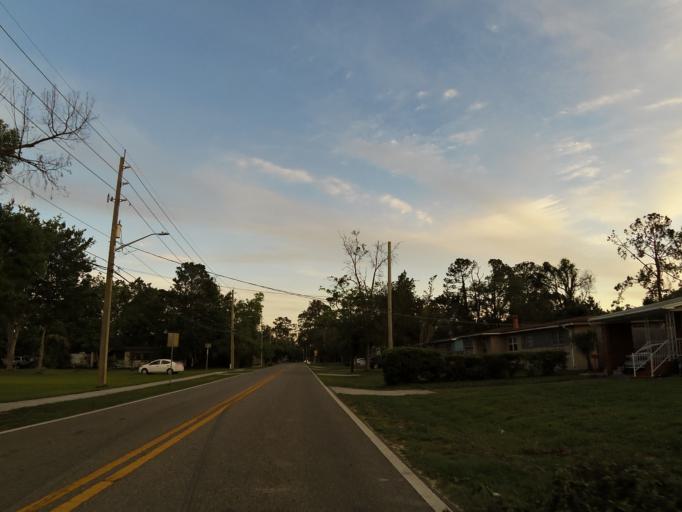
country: US
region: Florida
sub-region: Duval County
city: Jacksonville
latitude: 30.2827
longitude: -81.5920
